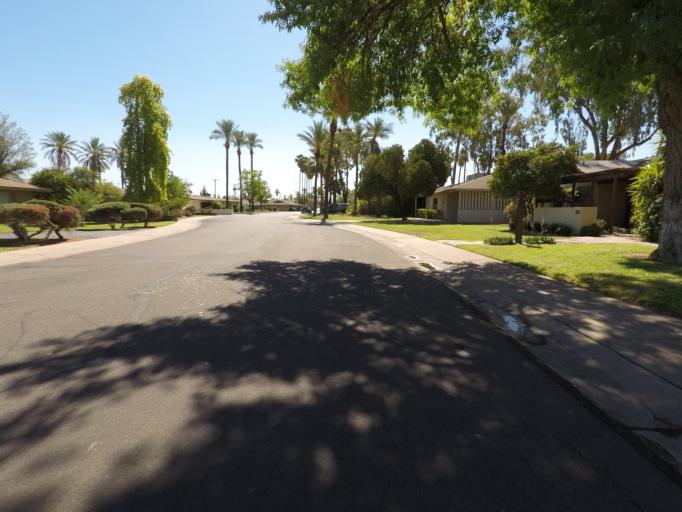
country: US
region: Arizona
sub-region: Maricopa County
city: Tempe Junction
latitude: 33.4059
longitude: -111.9409
